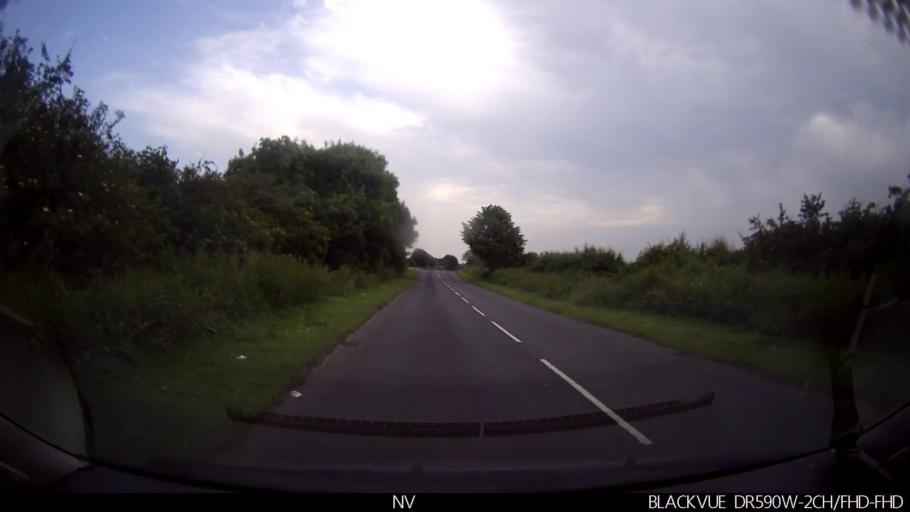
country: GB
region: England
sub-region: City of York
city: Copmanthorpe
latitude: 53.9429
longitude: -1.1419
